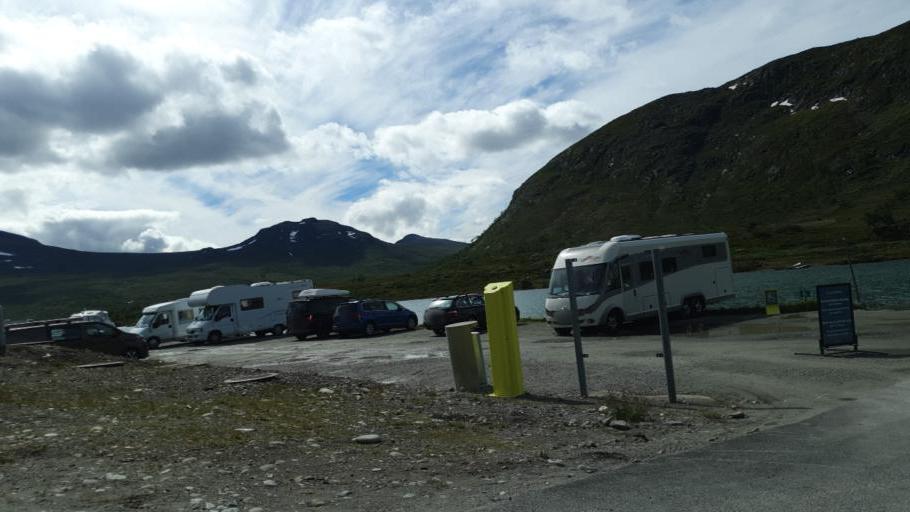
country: NO
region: Oppland
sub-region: Lom
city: Fossbergom
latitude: 61.4952
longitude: 8.8098
